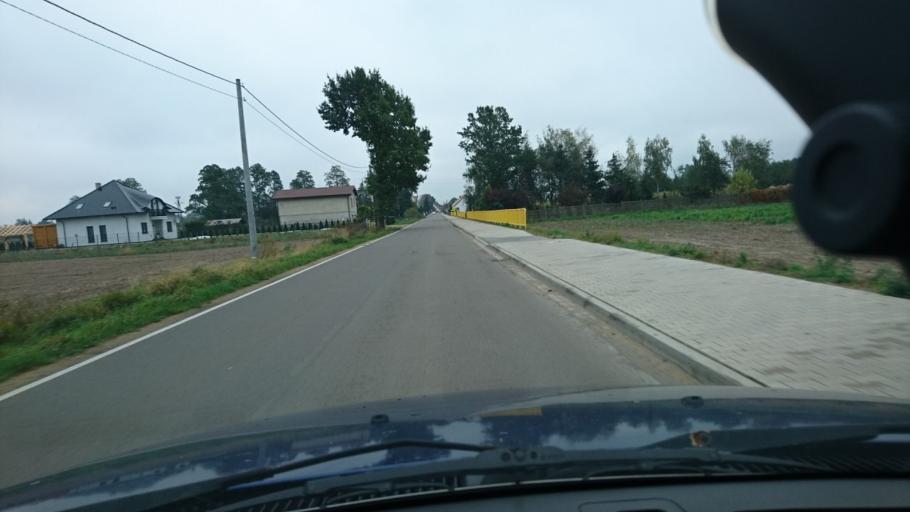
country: PL
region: Greater Poland Voivodeship
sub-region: Powiat ostrowski
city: Odolanow
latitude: 51.5739
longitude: 17.6202
